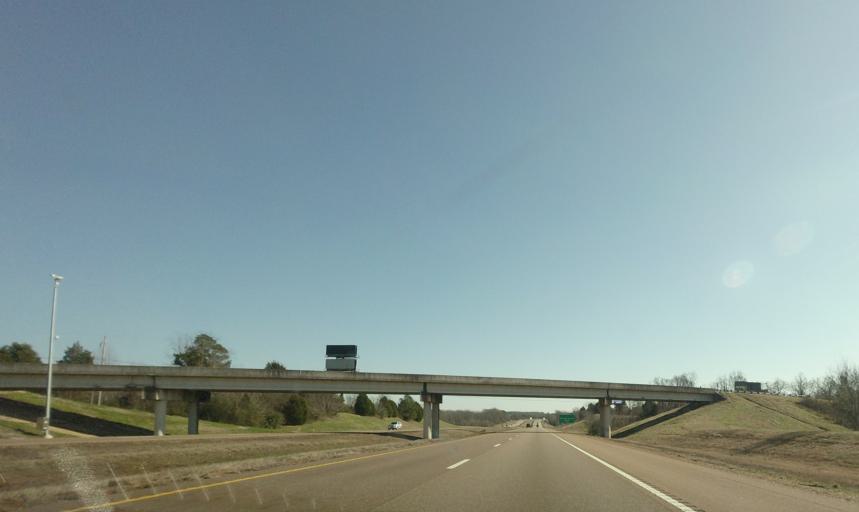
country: US
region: Mississippi
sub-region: Marshall County
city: Holly Springs
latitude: 34.8075
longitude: -89.5118
